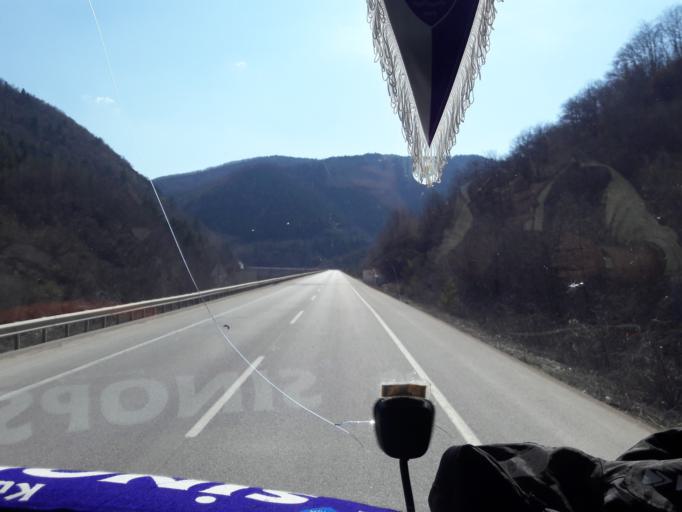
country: TR
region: Sinop
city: Erfelek
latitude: 41.6985
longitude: 34.9123
